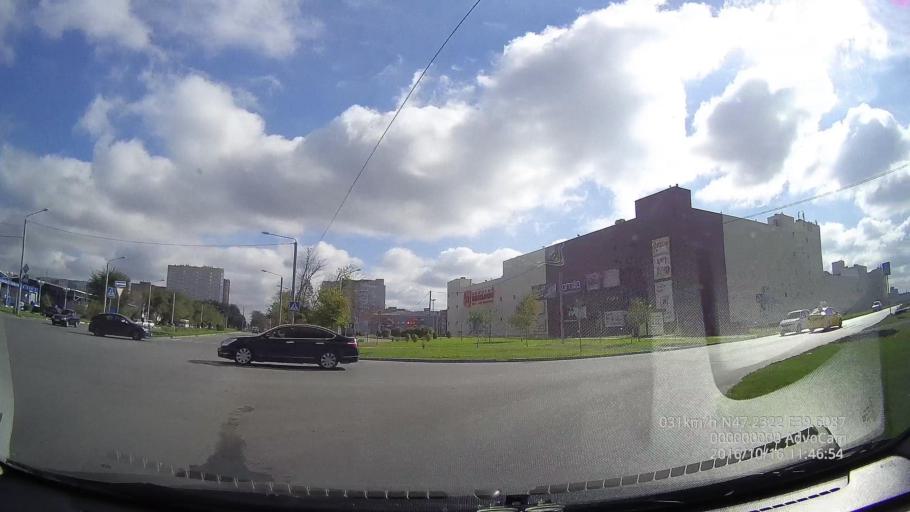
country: RU
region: Rostov
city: Kalinin
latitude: 47.2199
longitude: 39.6136
